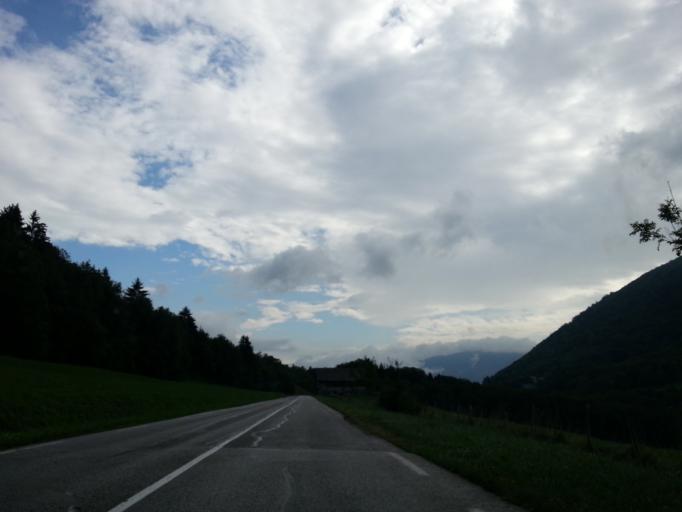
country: FR
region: Rhone-Alpes
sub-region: Departement de la Haute-Savoie
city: Dingy-Saint-Clair
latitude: 45.8806
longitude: 6.2201
